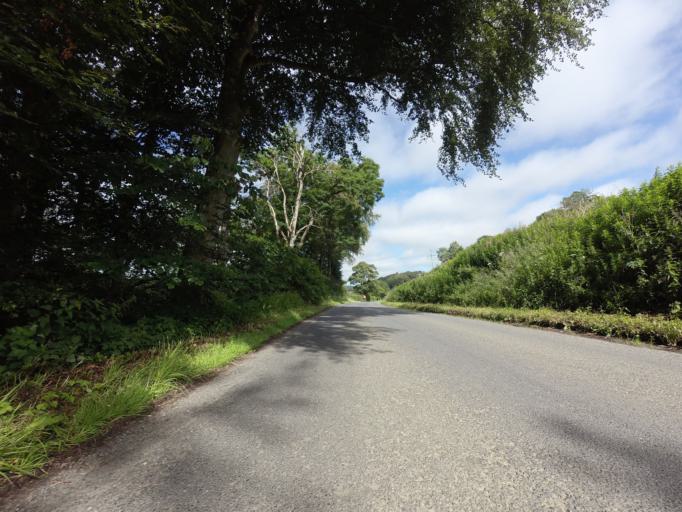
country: GB
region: Scotland
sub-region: Aberdeenshire
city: Turriff
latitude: 57.5436
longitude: -2.4786
